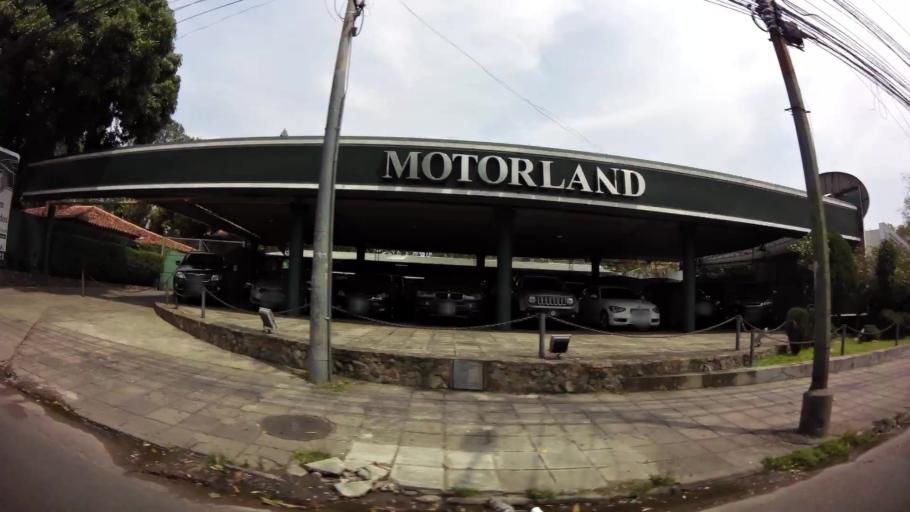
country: PY
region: Asuncion
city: Asuncion
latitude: -25.2867
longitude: -57.5898
